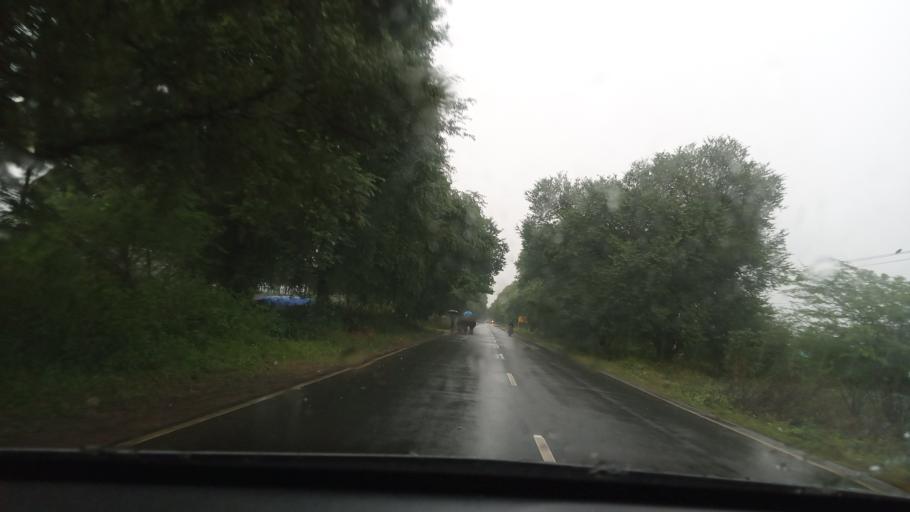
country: IN
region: Tamil Nadu
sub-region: Vellore
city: Kalavai
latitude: 12.8442
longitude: 79.3977
